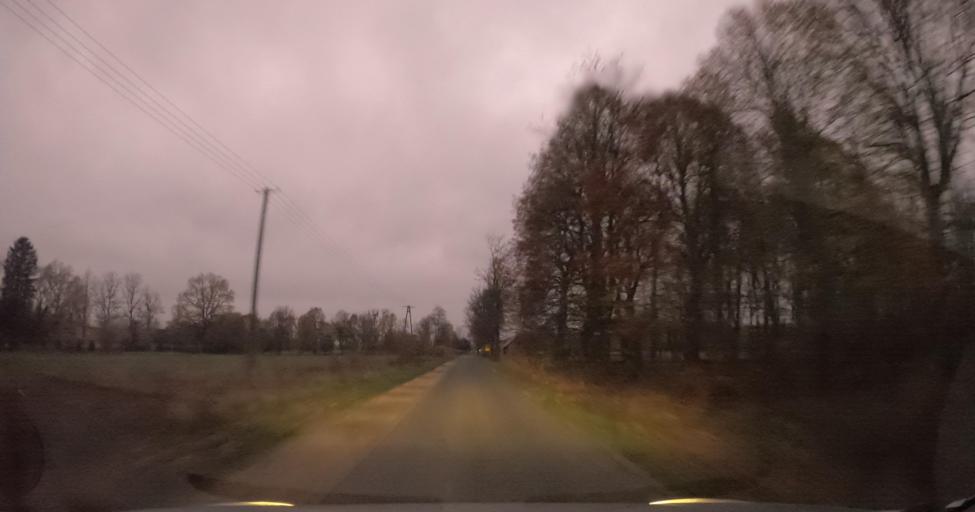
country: PL
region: West Pomeranian Voivodeship
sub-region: Powiat bialogardzki
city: Tychowo
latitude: 53.8735
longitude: 16.2345
